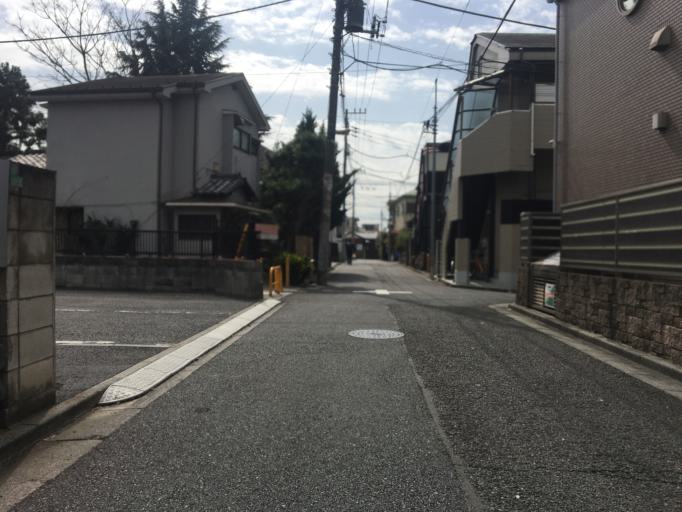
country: JP
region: Tokyo
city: Tokyo
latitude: 35.7414
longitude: 139.6753
